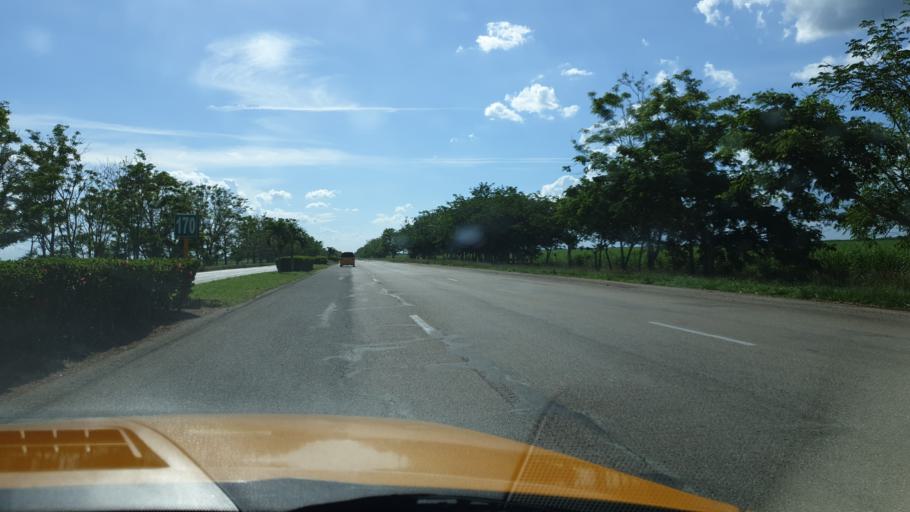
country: CU
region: Cienfuegos
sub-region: Municipio de Aguada de Pasajeros
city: Aguada de Pasajeros
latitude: 22.4121
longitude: -80.8972
